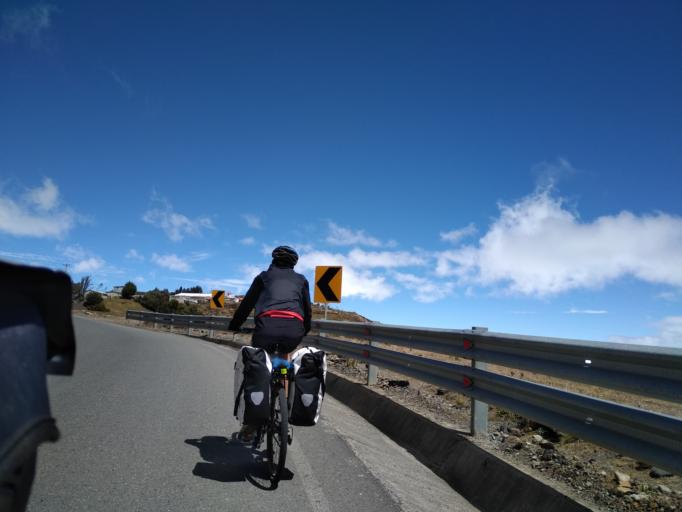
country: EC
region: Cotopaxi
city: Pujili
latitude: -0.9685
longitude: -78.9291
